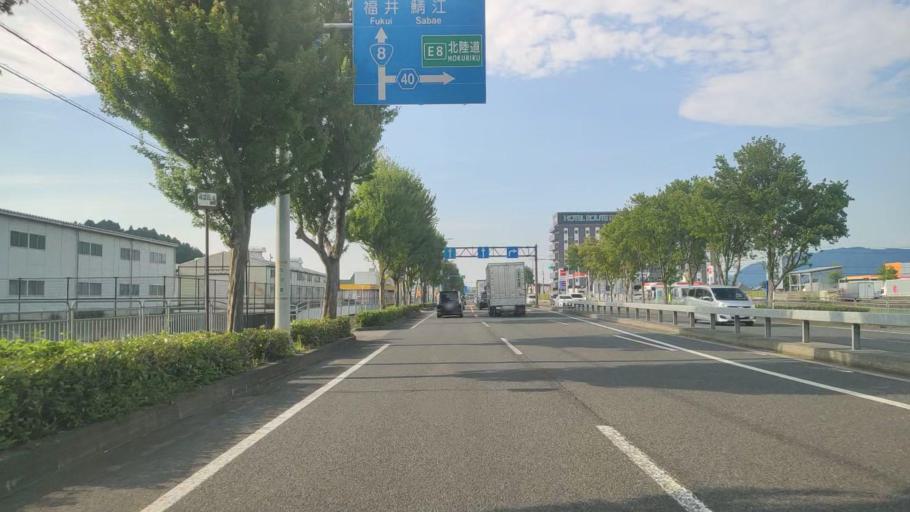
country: JP
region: Fukui
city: Takefu
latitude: 35.9009
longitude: 136.1922
